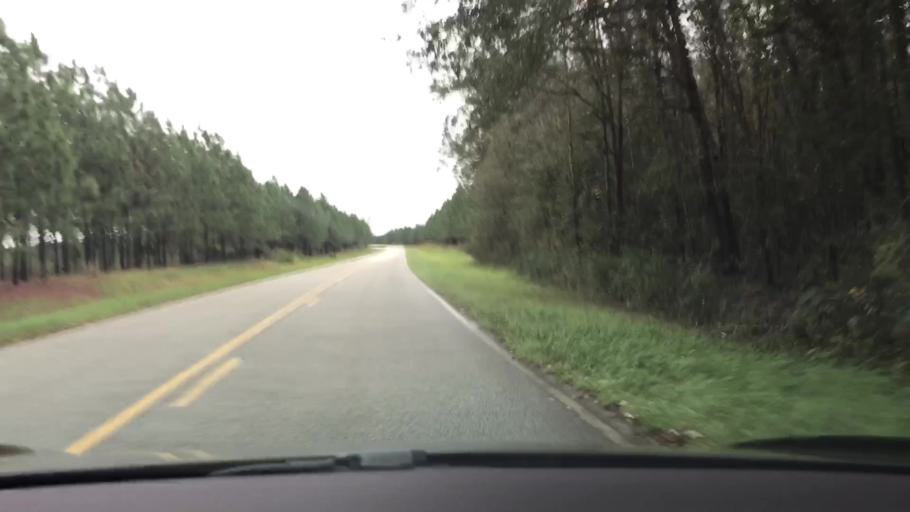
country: US
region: Georgia
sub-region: Jefferson County
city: Wadley
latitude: 32.8377
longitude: -82.3909
